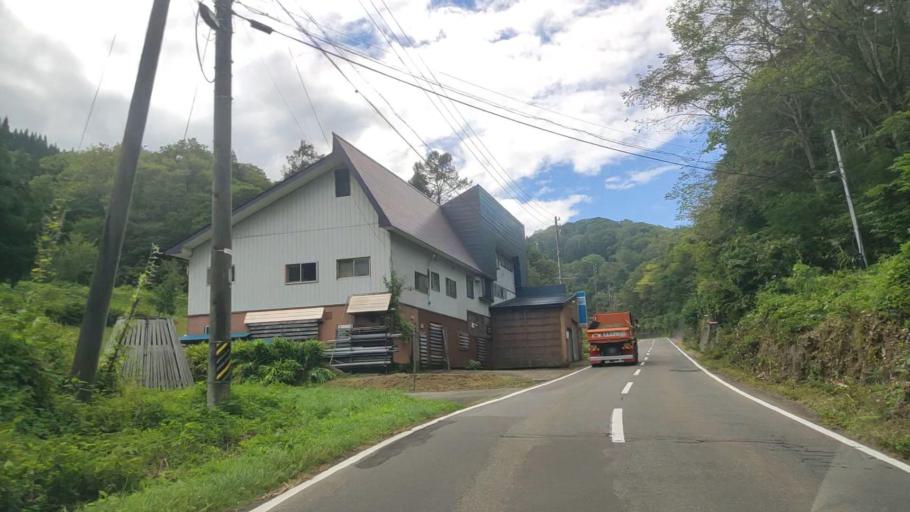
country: JP
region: Nagano
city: Iiyama
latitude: 36.8806
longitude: 138.3206
